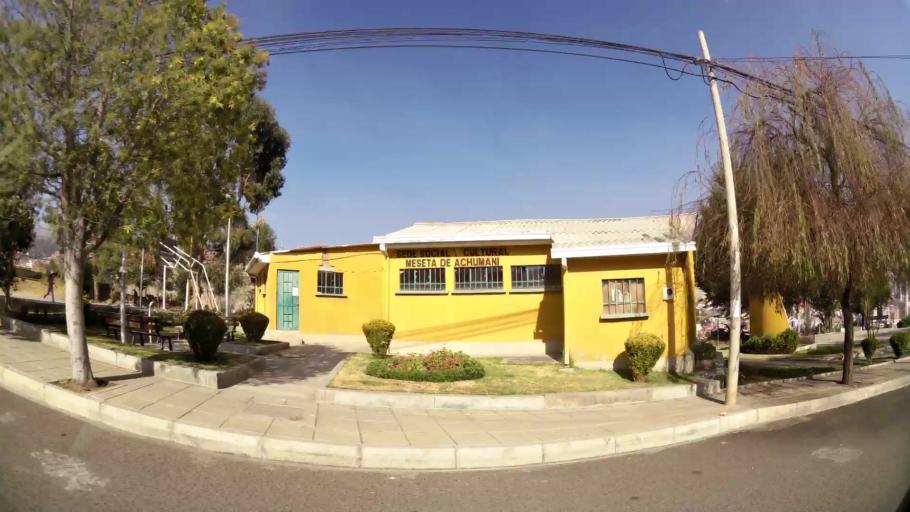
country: BO
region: La Paz
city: La Paz
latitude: -16.5288
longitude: -68.0760
